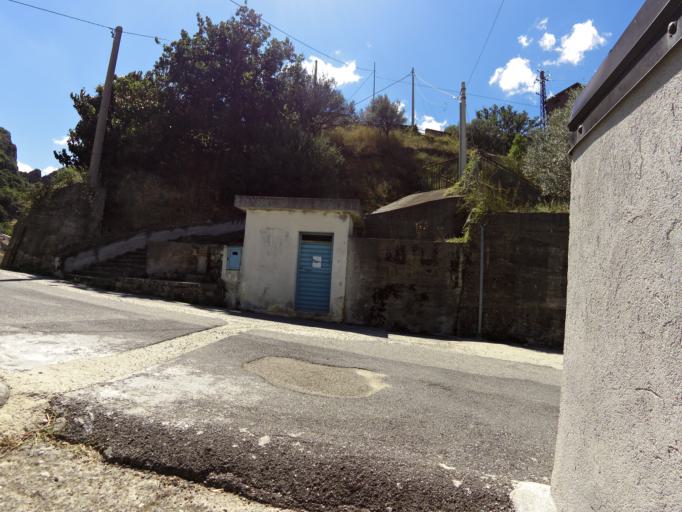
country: IT
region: Calabria
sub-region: Provincia di Reggio Calabria
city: Pazzano
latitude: 38.4776
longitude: 16.4498
